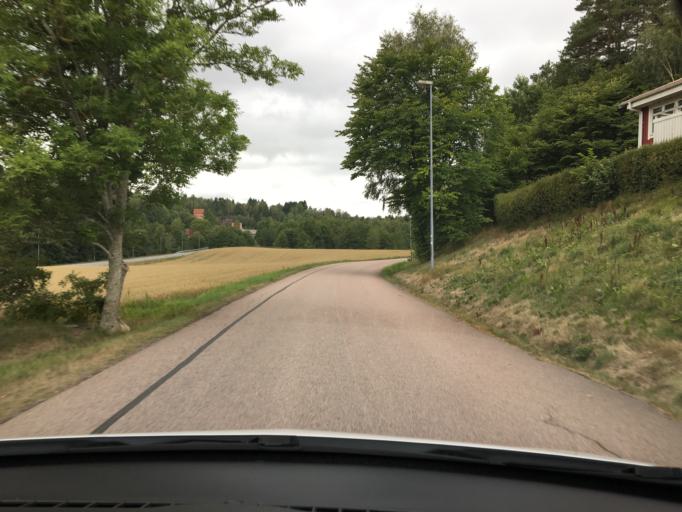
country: SE
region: Vaestra Goetaland
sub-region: Ale Kommun
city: Alafors
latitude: 57.9213
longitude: 12.0895
